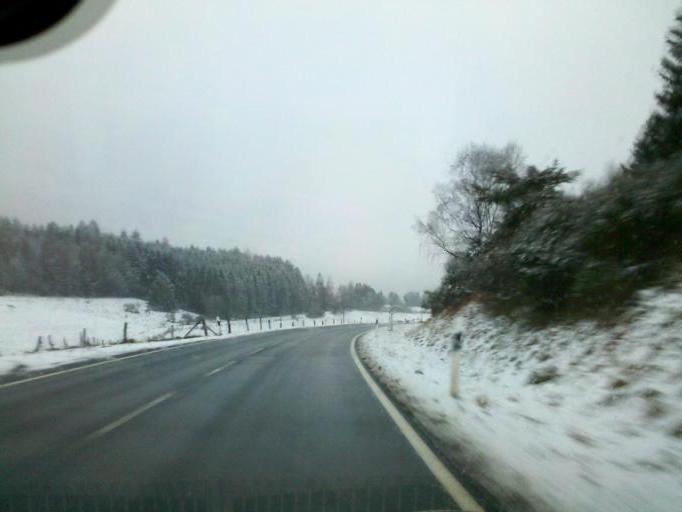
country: DE
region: Hesse
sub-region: Regierungsbezirk Giessen
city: Breidenbach
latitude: 50.8266
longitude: 8.4027
